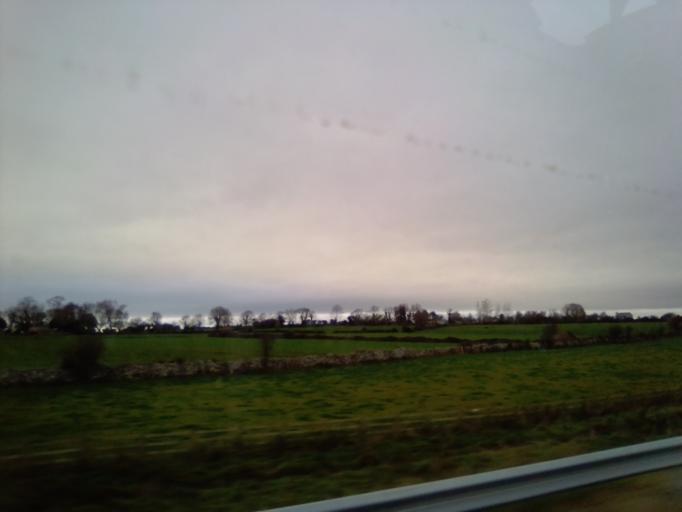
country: IE
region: Connaught
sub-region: County Galway
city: Oranmore
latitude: 53.2057
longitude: -8.8275
